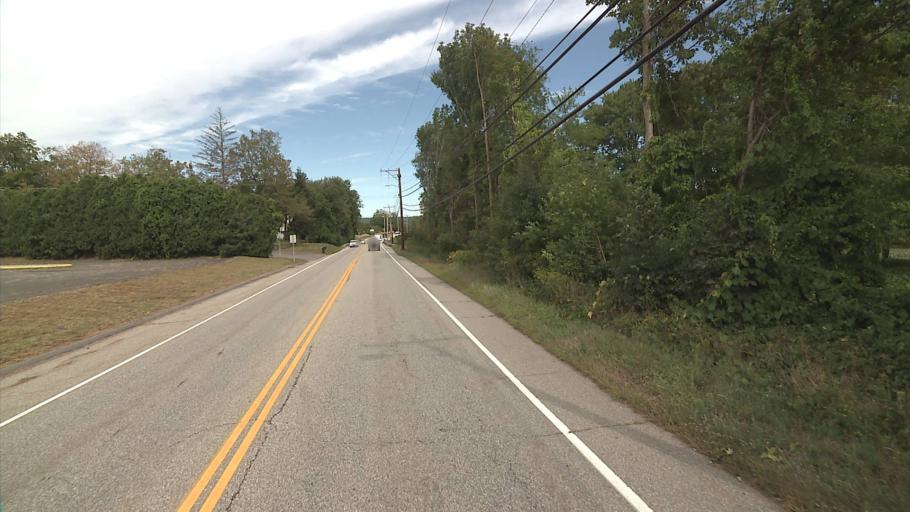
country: US
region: Connecticut
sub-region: Tolland County
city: Mansfield City
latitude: 41.7378
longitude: -72.2580
